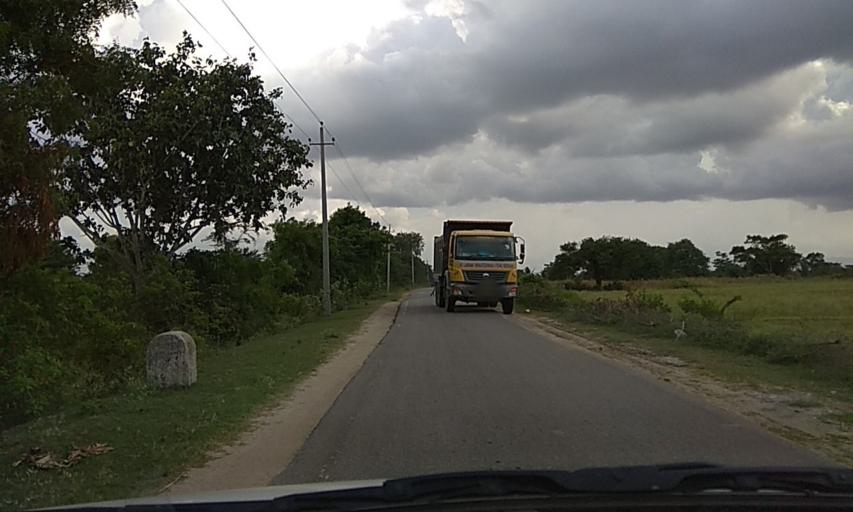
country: IN
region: Karnataka
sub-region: Chamrajnagar
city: Gundlupet
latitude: 11.8744
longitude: 76.7472
